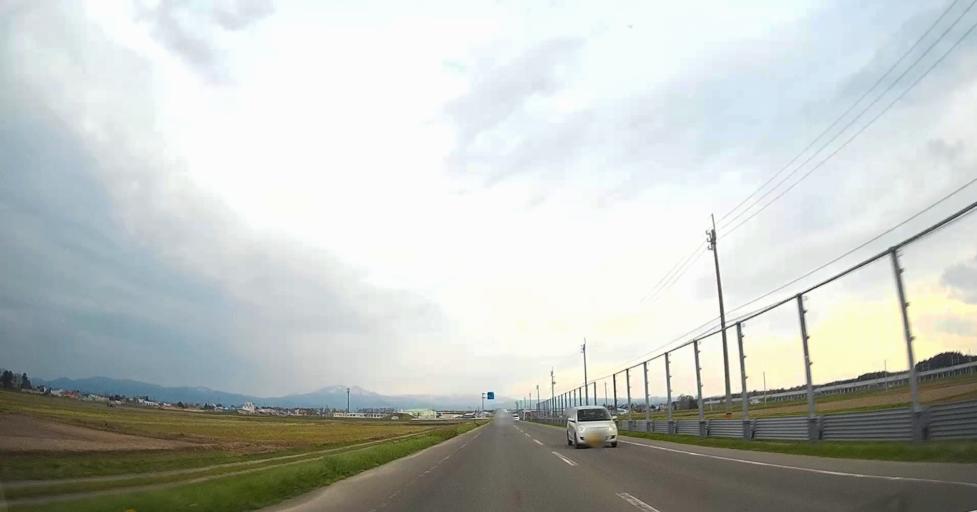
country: JP
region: Aomori
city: Aomori Shi
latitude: 40.8660
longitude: 140.6790
